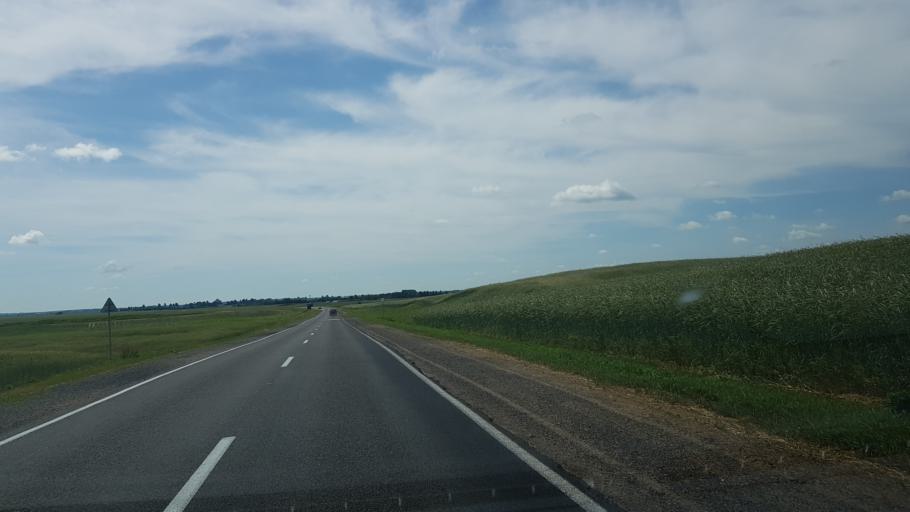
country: BY
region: Vitebsk
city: Dubrowna
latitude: 54.6352
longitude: 30.6633
